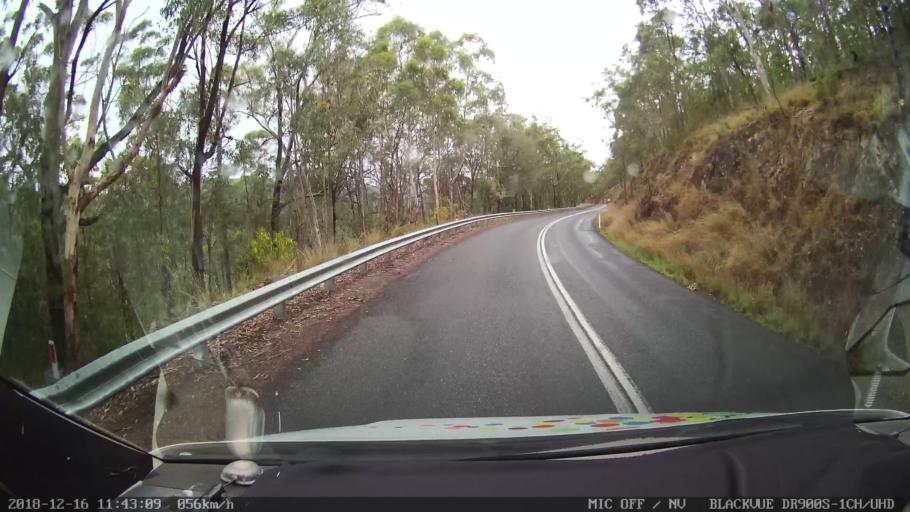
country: AU
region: New South Wales
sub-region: Tenterfield Municipality
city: Carrolls Creek
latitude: -28.9476
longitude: 152.2152
